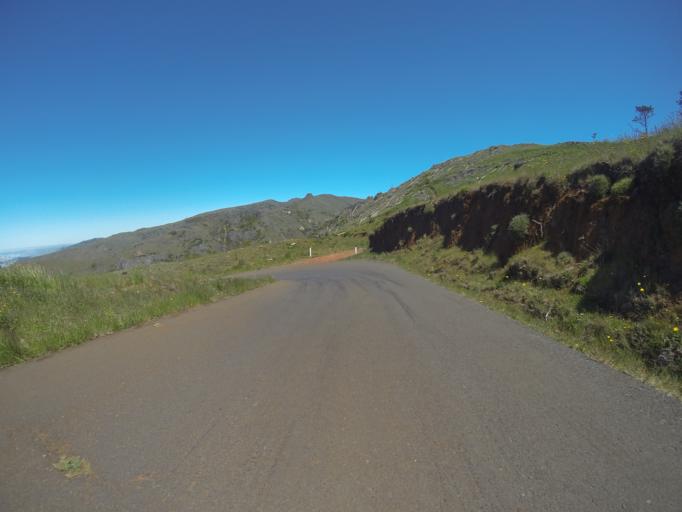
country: PT
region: Madeira
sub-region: Funchal
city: Nossa Senhora do Monte
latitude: 32.7081
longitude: -16.9140
